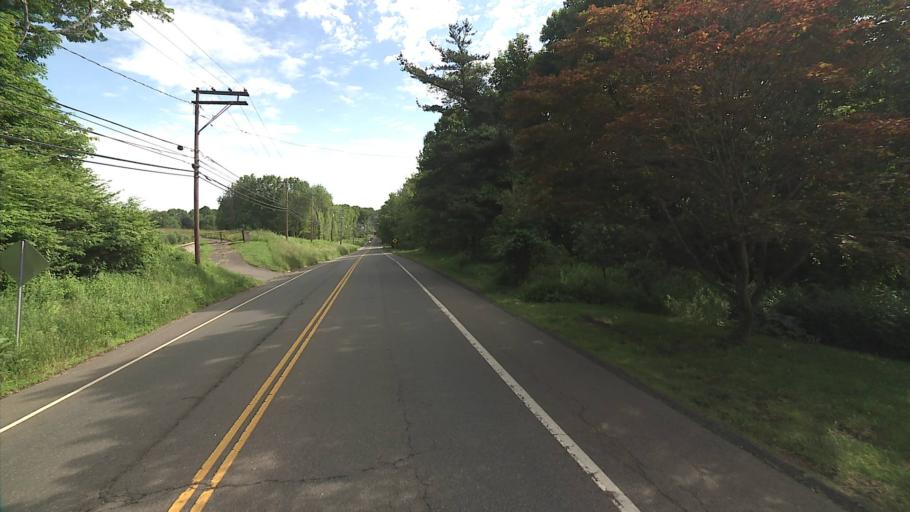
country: US
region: Connecticut
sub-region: New Haven County
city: Woodbridge
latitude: 41.4171
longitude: -72.9984
